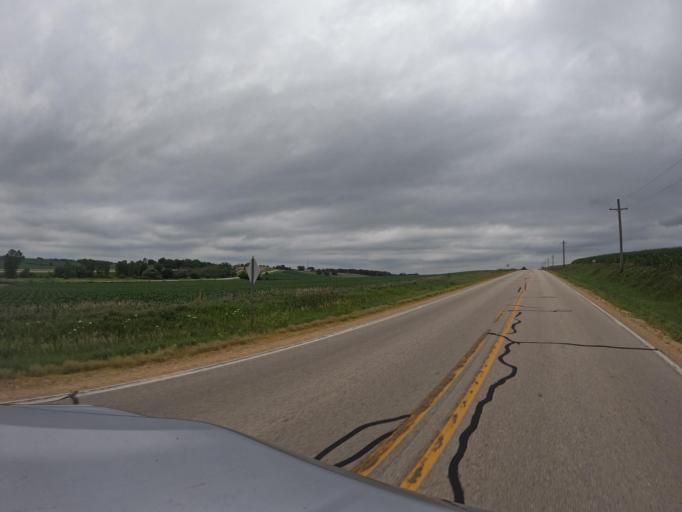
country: US
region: Iowa
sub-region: Clinton County
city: De Witt
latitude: 41.9321
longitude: -90.6066
